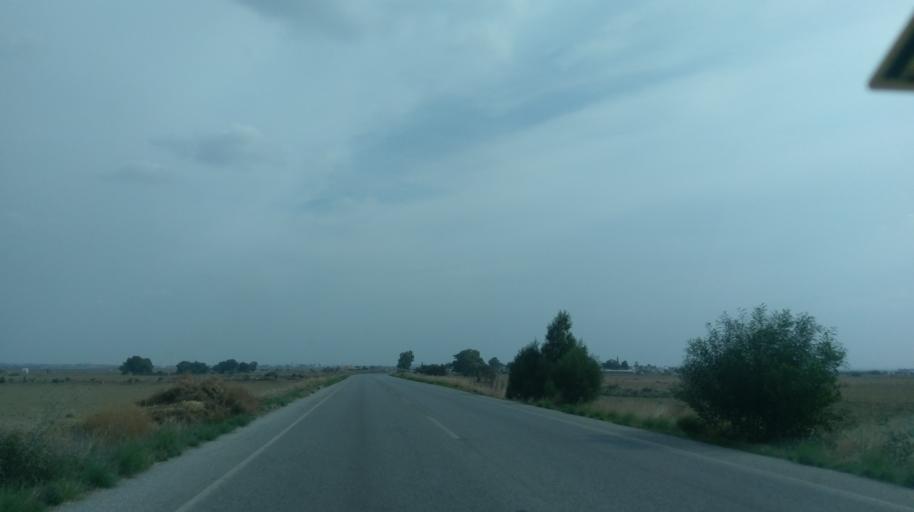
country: CY
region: Ammochostos
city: Lefkonoiko
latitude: 35.2582
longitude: 33.6764
